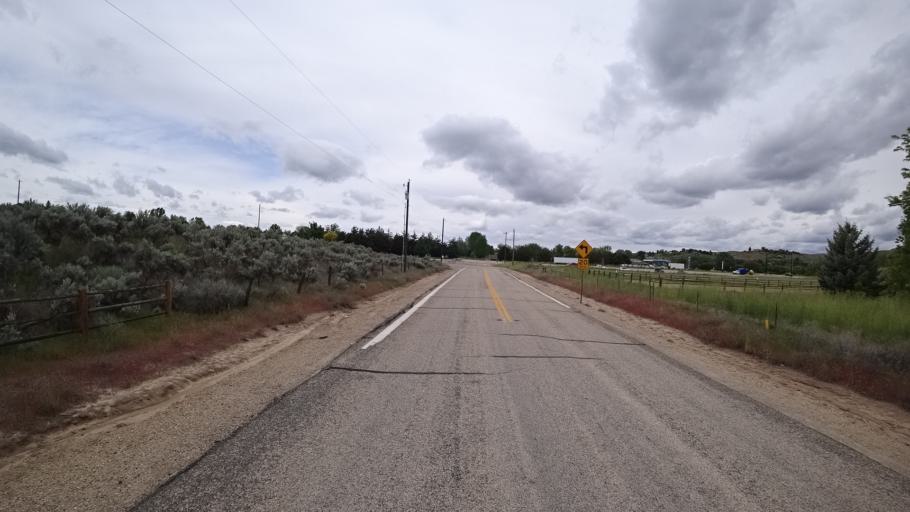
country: US
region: Idaho
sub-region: Ada County
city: Eagle
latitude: 43.7191
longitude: -116.3182
